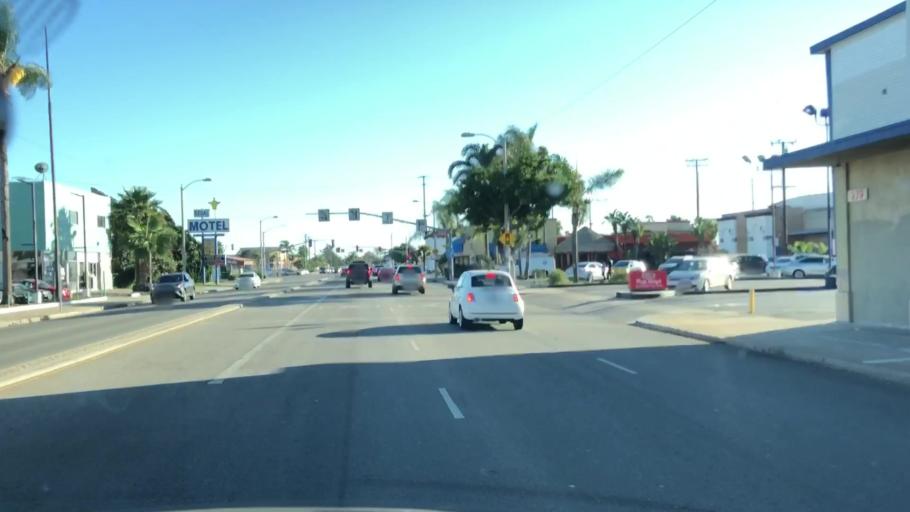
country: US
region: California
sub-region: Ventura County
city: Oxnard
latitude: 34.1917
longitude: -119.1775
